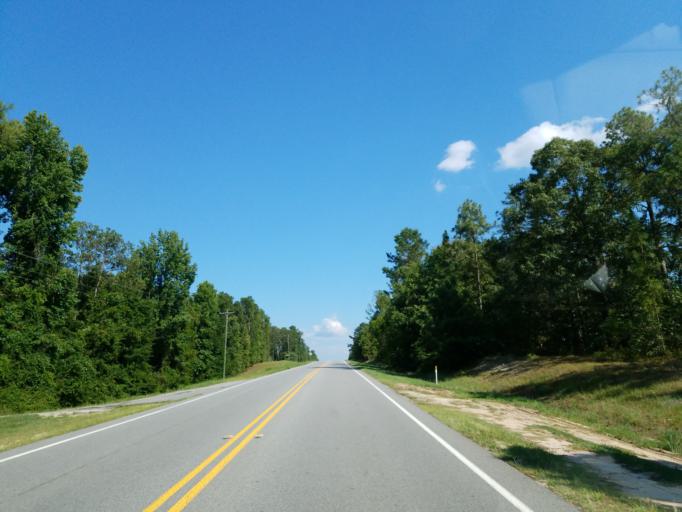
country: US
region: Georgia
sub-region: Crawford County
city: Knoxville
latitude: 32.6529
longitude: -83.9836
